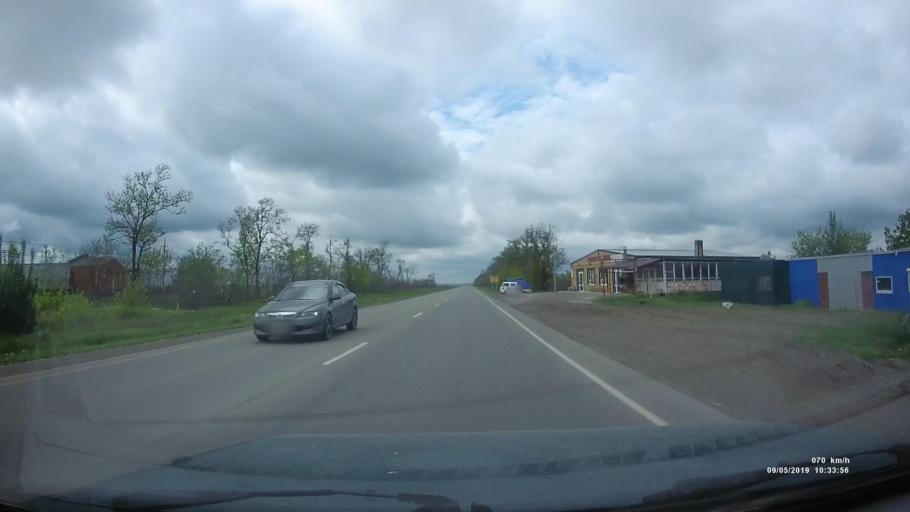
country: RU
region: Rostov
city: Azov
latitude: 47.0594
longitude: 39.4230
